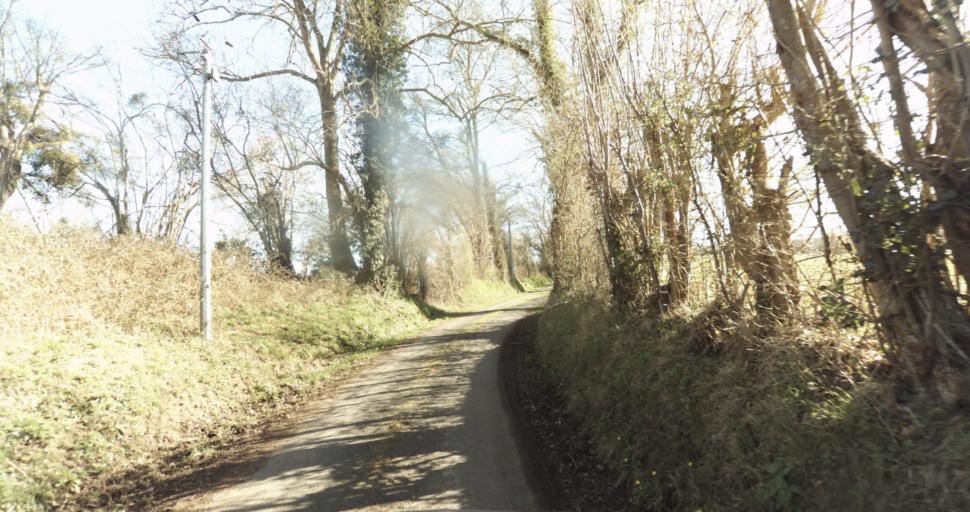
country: FR
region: Lower Normandy
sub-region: Departement du Calvados
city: Livarot
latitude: 49.0261
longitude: 0.0663
